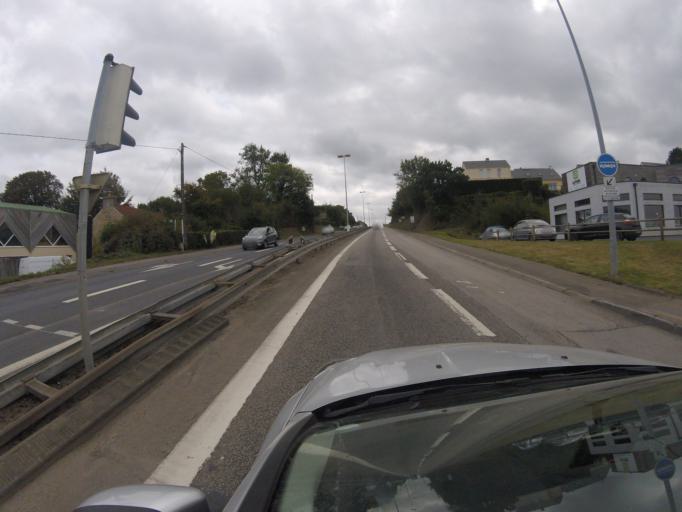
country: FR
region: Lower Normandy
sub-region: Departement de la Manche
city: La Glacerie
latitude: 49.6120
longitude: -1.6010
